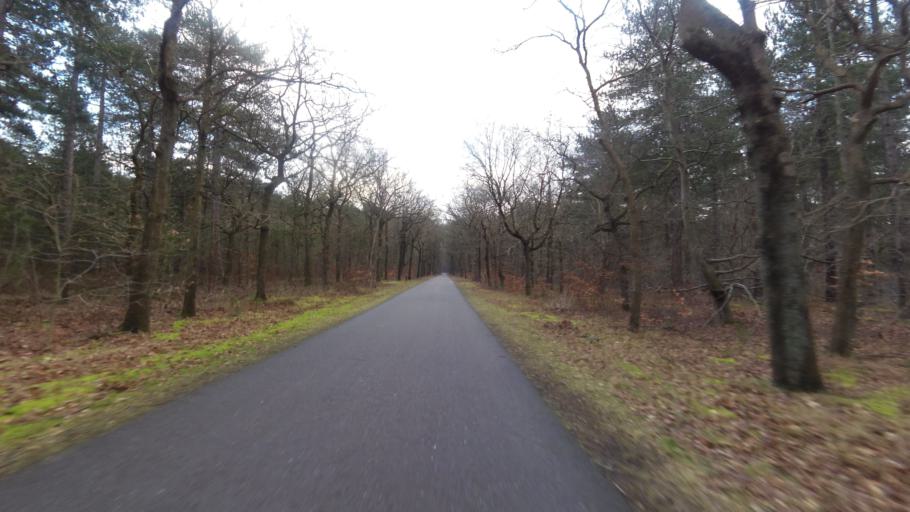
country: NL
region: North Holland
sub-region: Gemeente Bergen
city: Egmond aan Zee
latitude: 52.6867
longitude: 4.6662
